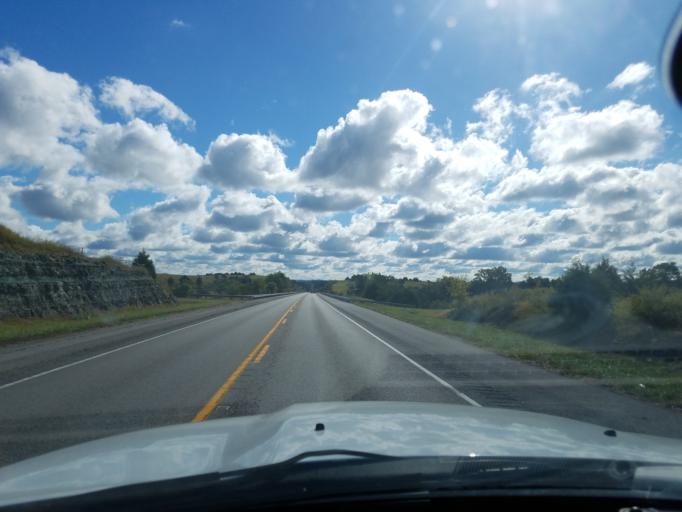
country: US
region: Kentucky
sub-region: Lincoln County
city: Stanford
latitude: 37.5132
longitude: -84.5988
